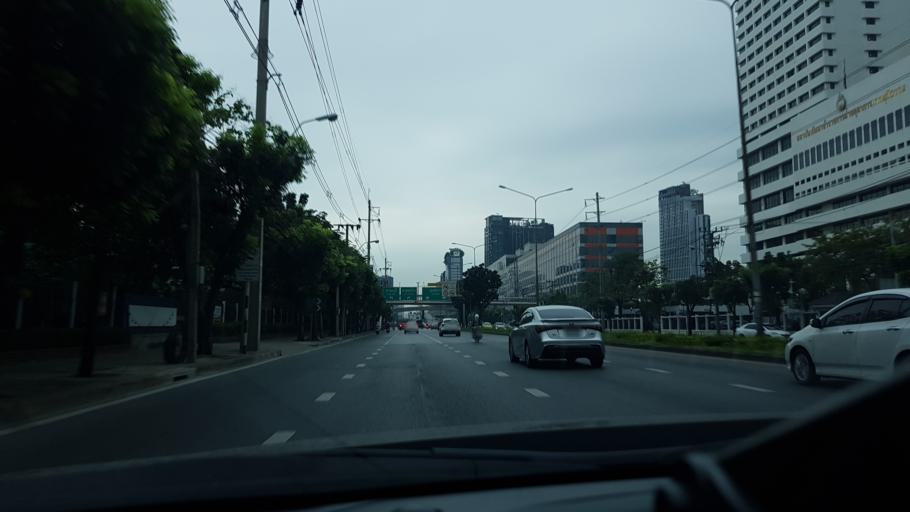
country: TH
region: Bangkok
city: Chatuchak
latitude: 13.8116
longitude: 100.5754
